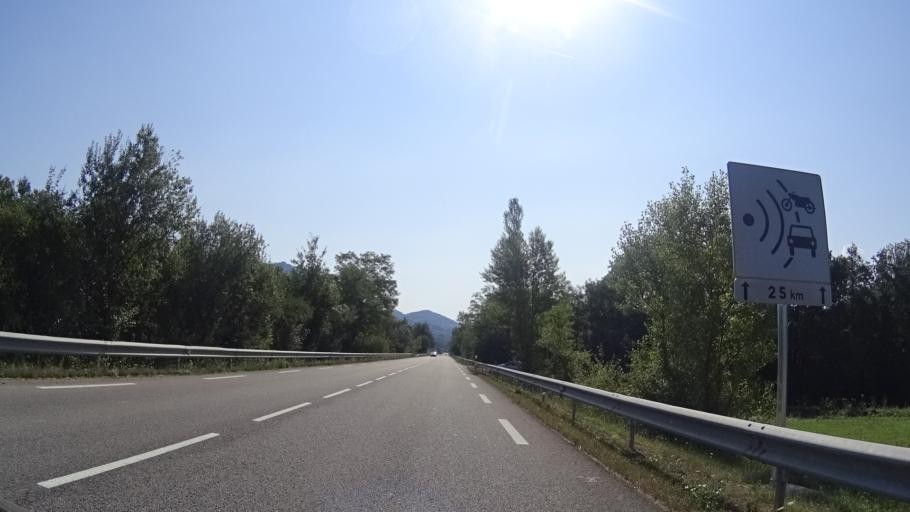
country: FR
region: Midi-Pyrenees
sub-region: Departement de l'Ariege
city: Saint-Paul-de-Jarrat
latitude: 42.9336
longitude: 1.7162
